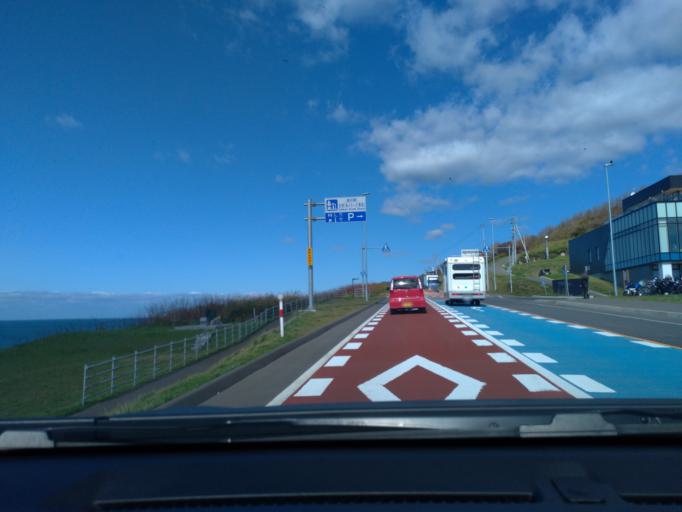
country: JP
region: Hokkaido
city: Ishikari
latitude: 43.4036
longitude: 141.4311
